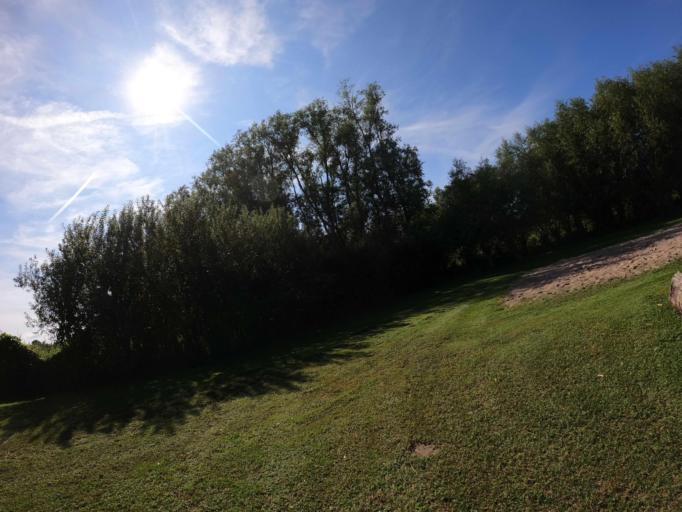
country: DE
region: Mecklenburg-Vorpommern
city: Prohn
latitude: 54.3826
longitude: 13.0435
